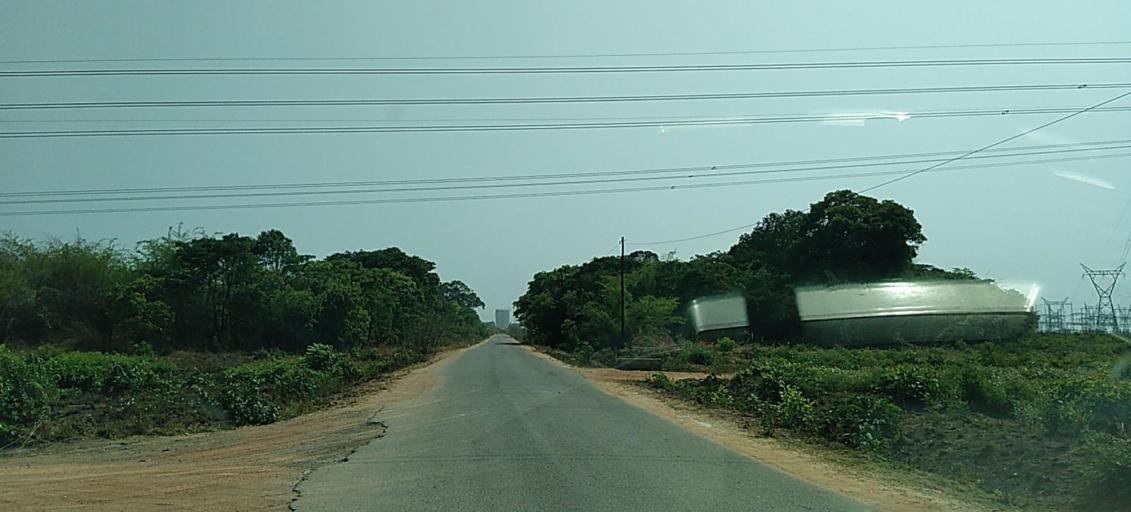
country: ZM
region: Copperbelt
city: Chambishi
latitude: -12.6051
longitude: 27.9739
